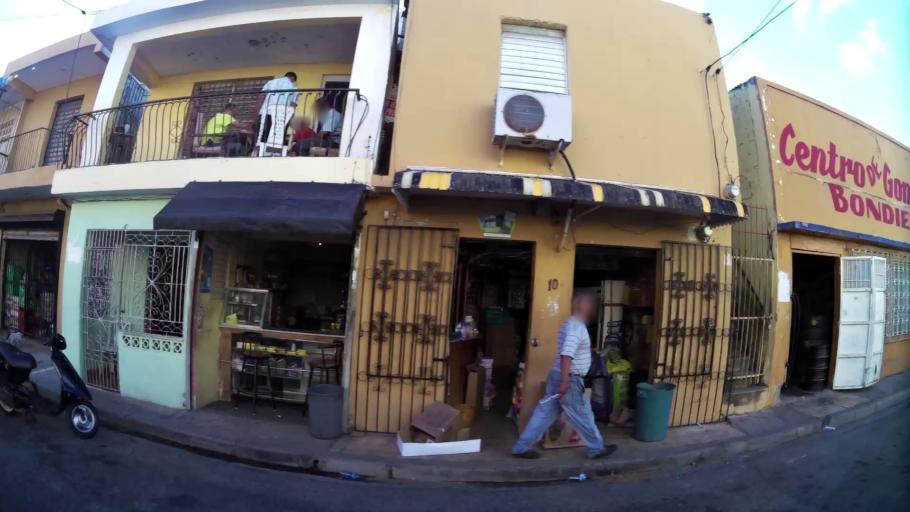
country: DO
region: Santiago
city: Santiago de los Caballeros
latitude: 19.4716
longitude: -70.7111
